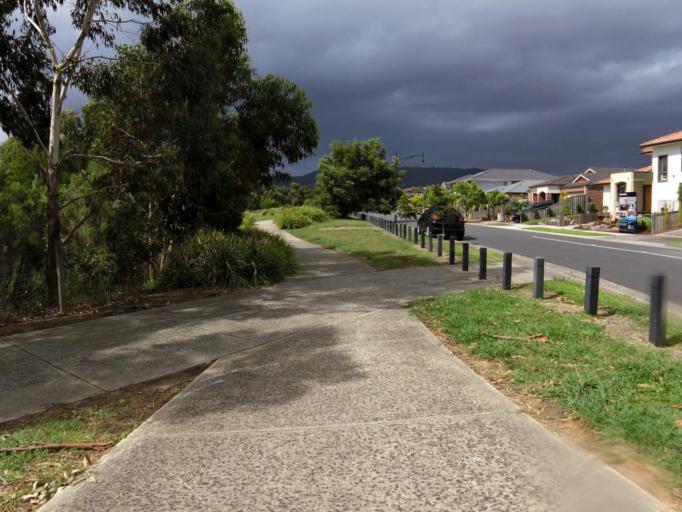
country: AU
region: Victoria
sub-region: Knox
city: Ferntree Gully
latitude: -37.9013
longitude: 145.2749
